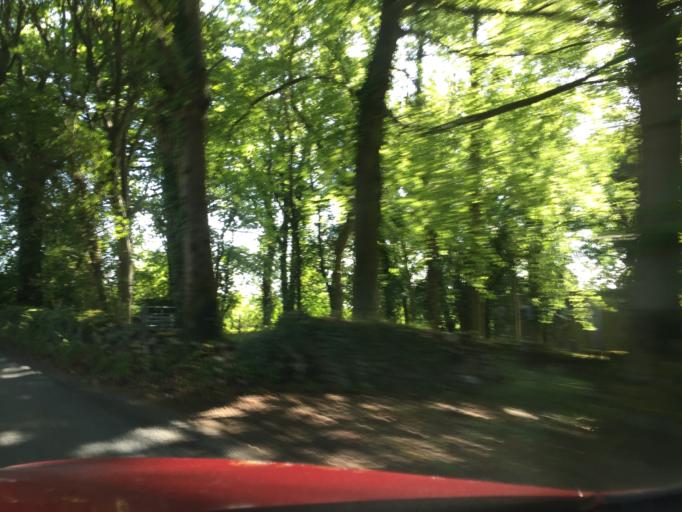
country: GB
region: England
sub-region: Gloucestershire
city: Stroud
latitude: 51.7682
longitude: -2.2388
